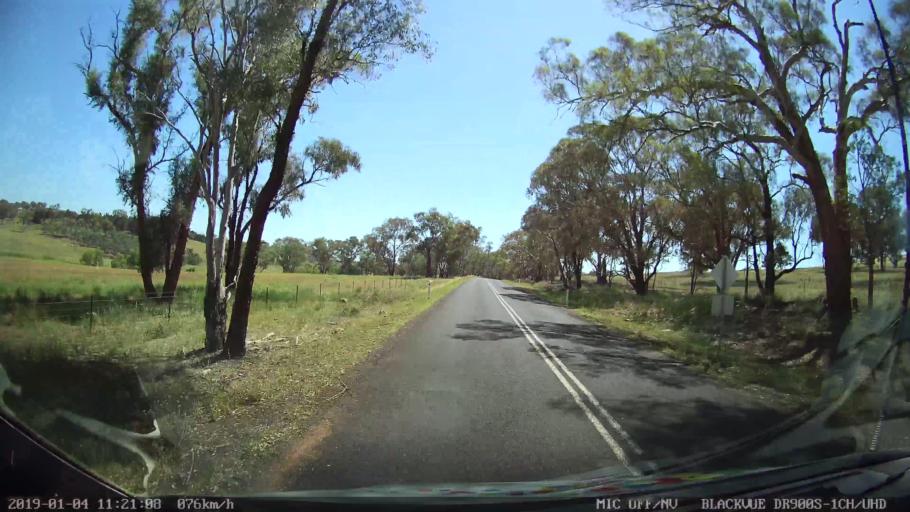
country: AU
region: New South Wales
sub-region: Cabonne
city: Molong
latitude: -33.1567
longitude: 148.7075
